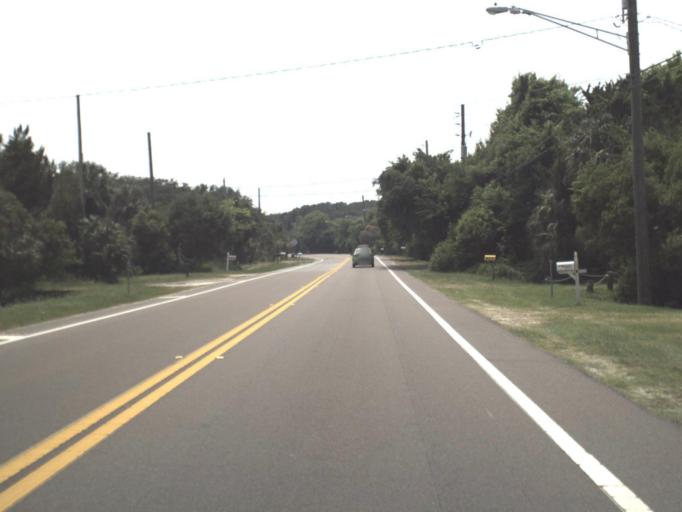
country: US
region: Florida
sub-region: Duval County
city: Atlantic Beach
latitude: 30.4066
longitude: -81.4281
